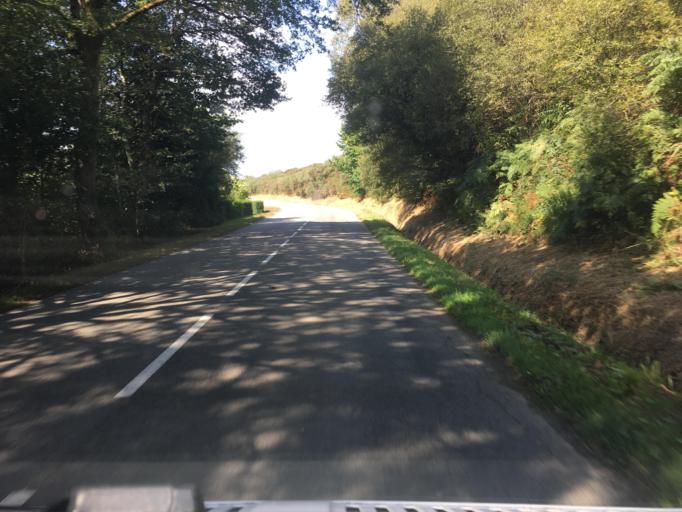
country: FR
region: Brittany
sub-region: Departement des Cotes-d'Armor
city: Mur-de-Bretagne
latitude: 48.2184
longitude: -3.0572
